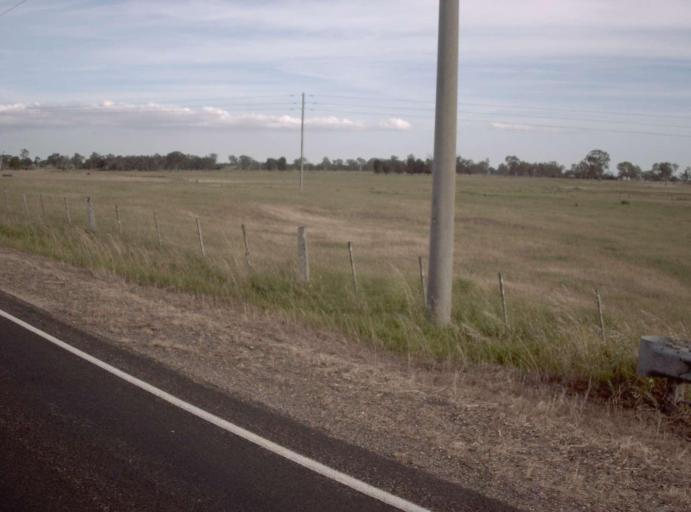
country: AU
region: Victoria
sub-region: Wellington
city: Heyfield
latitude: -37.9838
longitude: 146.8272
